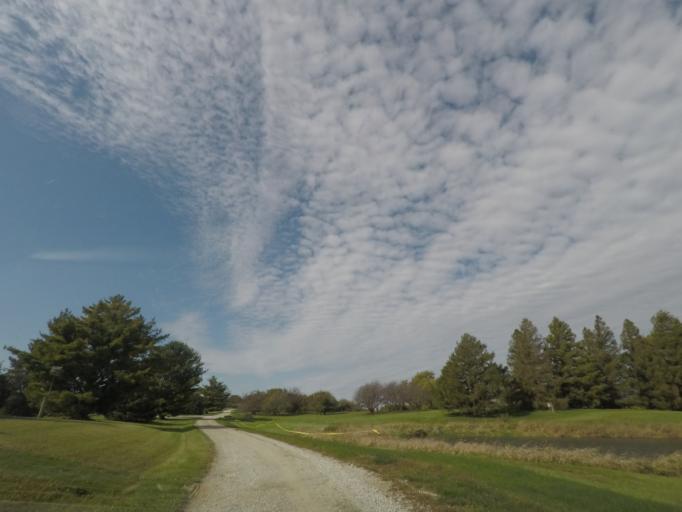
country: US
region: Iowa
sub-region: Story County
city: Gilbert
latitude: 42.1096
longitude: -93.5834
